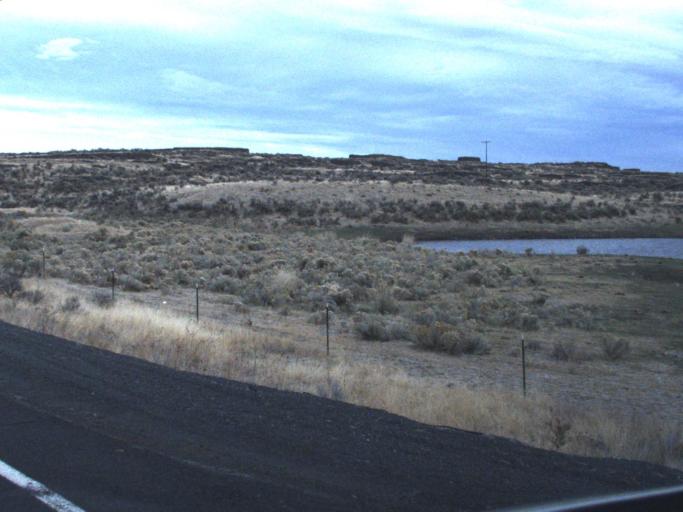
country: US
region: Washington
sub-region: Adams County
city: Ritzville
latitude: 47.4645
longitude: -118.7664
